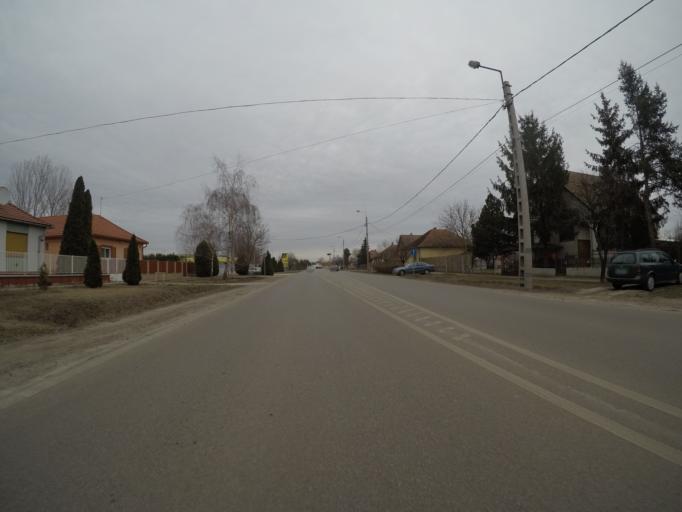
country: HU
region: Jasz-Nagykun-Szolnok
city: Jaszjakohalma
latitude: 47.5227
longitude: 19.9981
